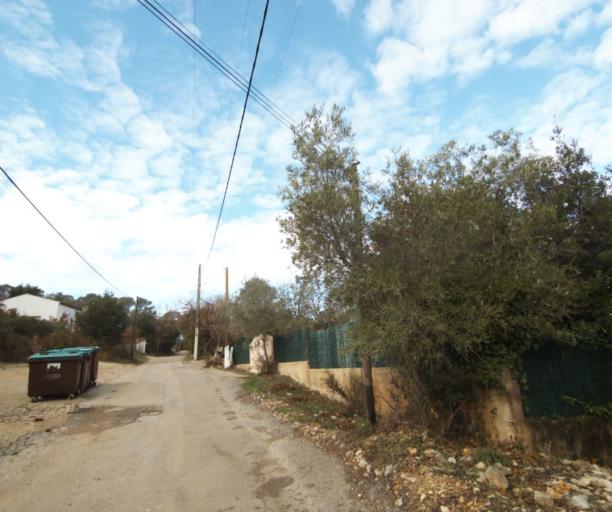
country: FR
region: Provence-Alpes-Cote d'Azur
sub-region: Departement du Var
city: Trans-en-Provence
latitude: 43.5018
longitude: 6.4769
